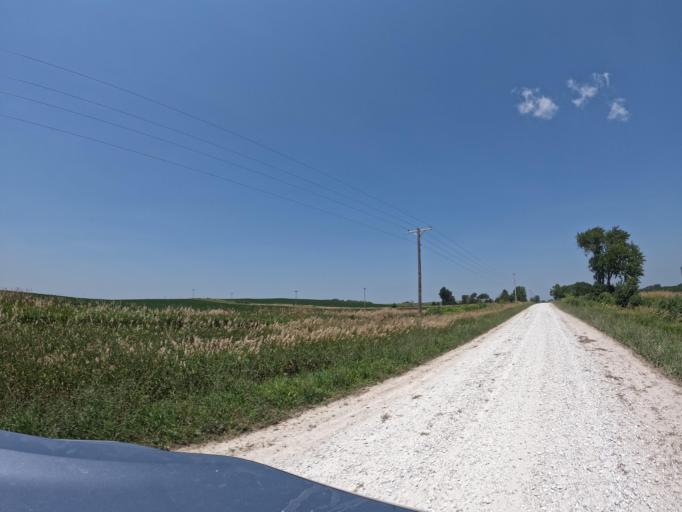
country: US
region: Iowa
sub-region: Keokuk County
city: Sigourney
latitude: 41.2929
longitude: -92.2095
